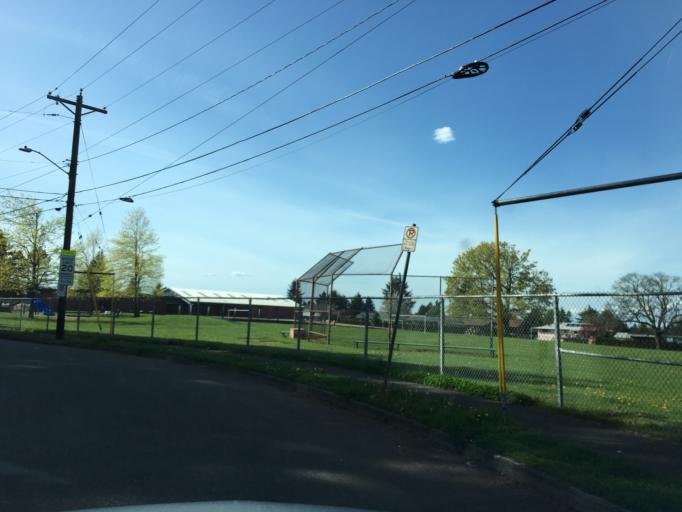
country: US
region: Oregon
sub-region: Multnomah County
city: Lents
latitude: 45.5408
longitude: -122.5293
